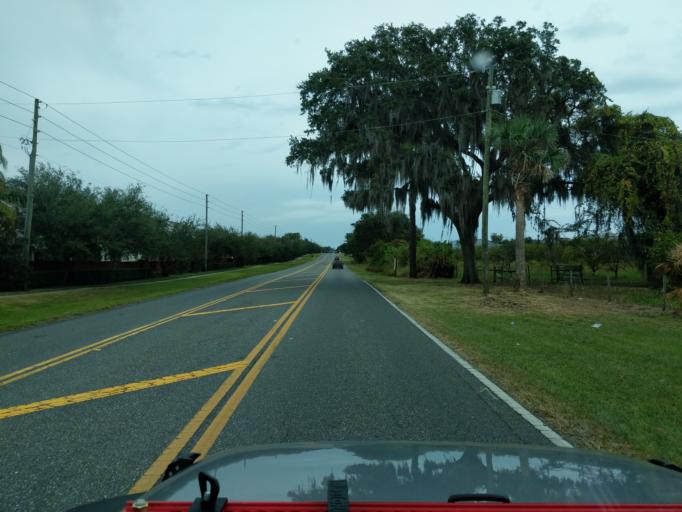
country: US
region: Florida
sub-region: Orange County
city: Oakland
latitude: 28.5333
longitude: -81.6080
